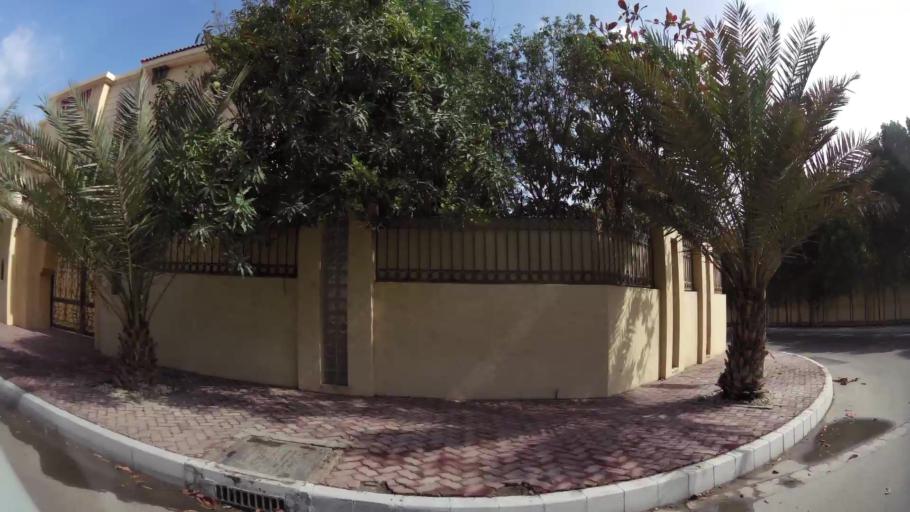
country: AE
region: Abu Dhabi
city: Abu Dhabi
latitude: 24.4426
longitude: 54.3609
